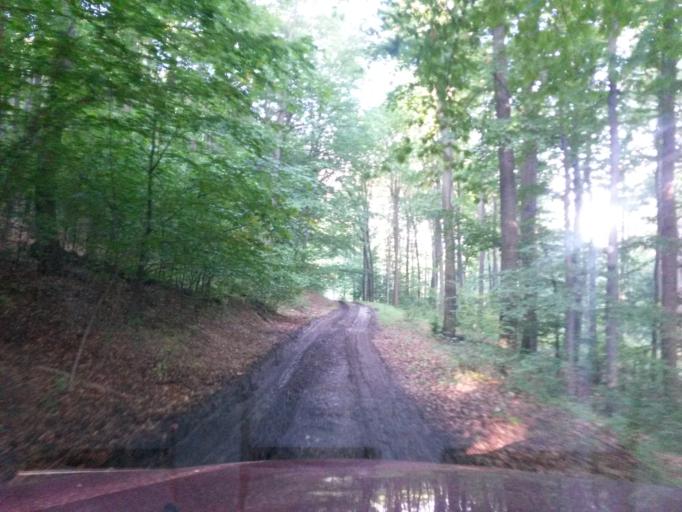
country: SK
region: Kosicky
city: Moldava nad Bodvou
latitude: 48.7294
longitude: 21.0546
